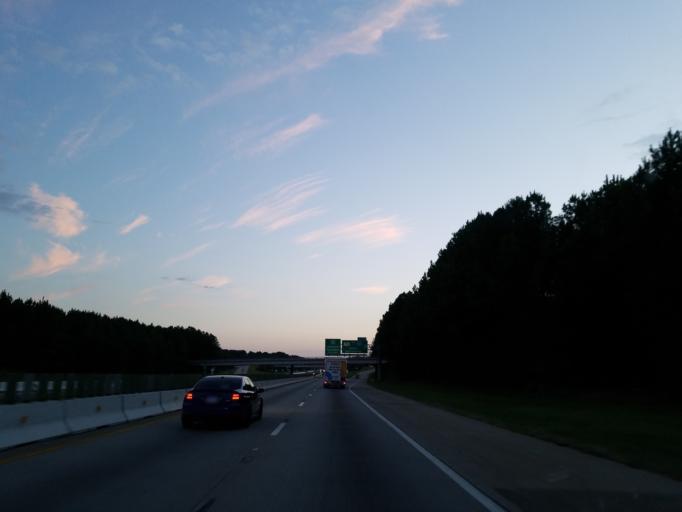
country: US
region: South Carolina
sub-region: Spartanburg County
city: Southern Shops
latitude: 35.0019
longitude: -81.9880
